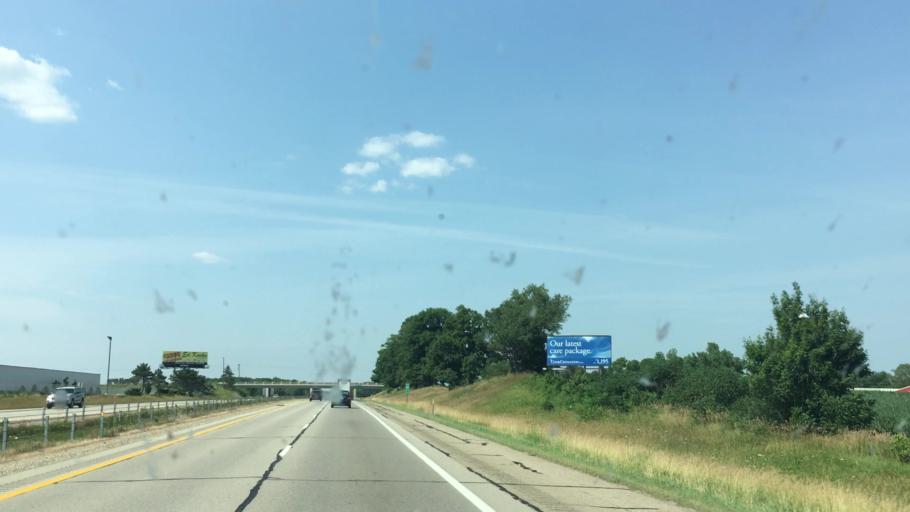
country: US
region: Michigan
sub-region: Allegan County
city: Wayland
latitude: 42.7362
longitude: -85.6732
